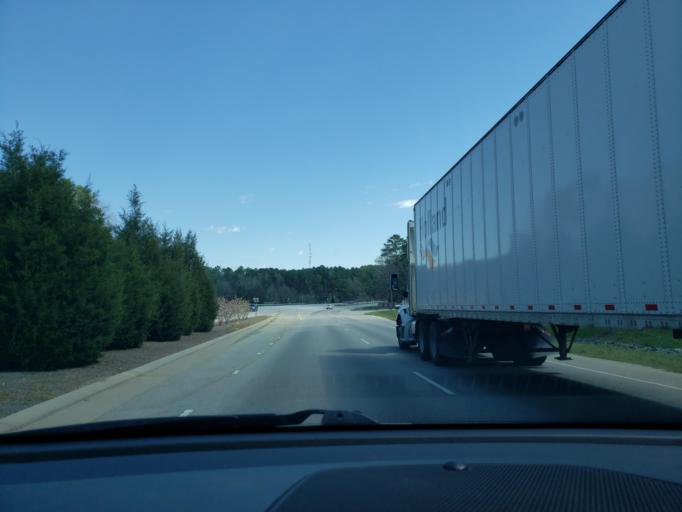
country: US
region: North Carolina
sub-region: Durham County
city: Durham
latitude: 35.9225
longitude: -78.8730
